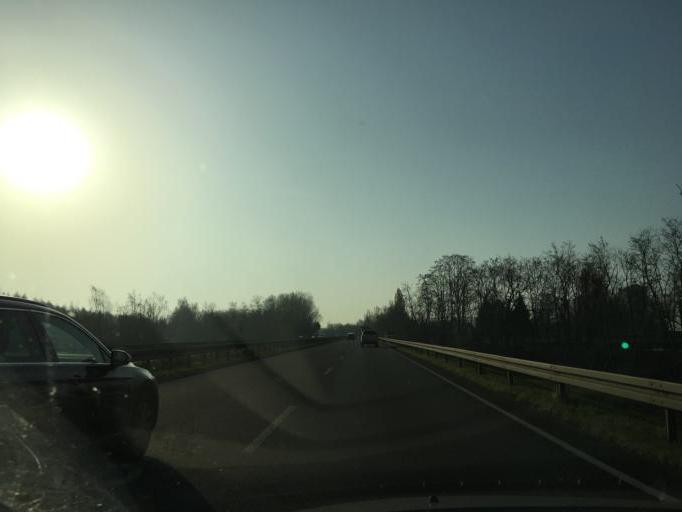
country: DE
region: Saxony
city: Rotha
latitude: 51.2027
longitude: 12.4175
